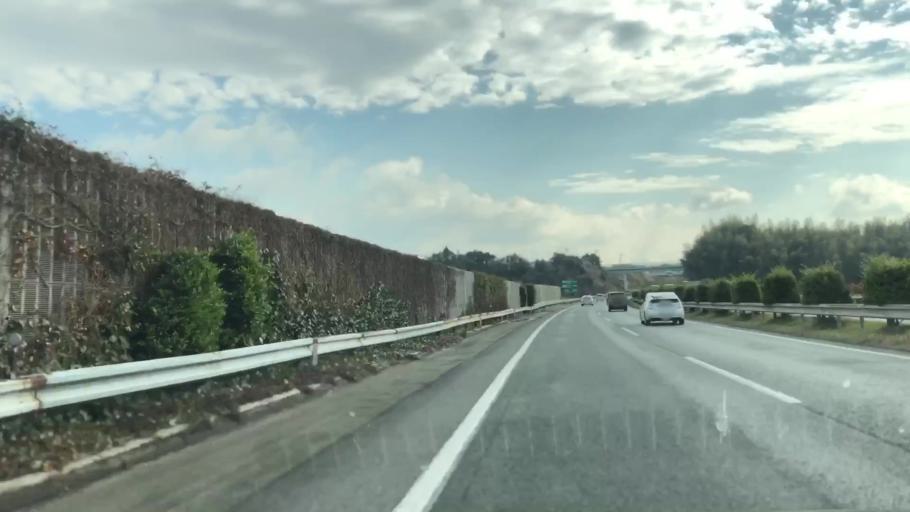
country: JP
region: Fukuoka
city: Setakamachi-takayanagi
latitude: 33.1362
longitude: 130.5157
